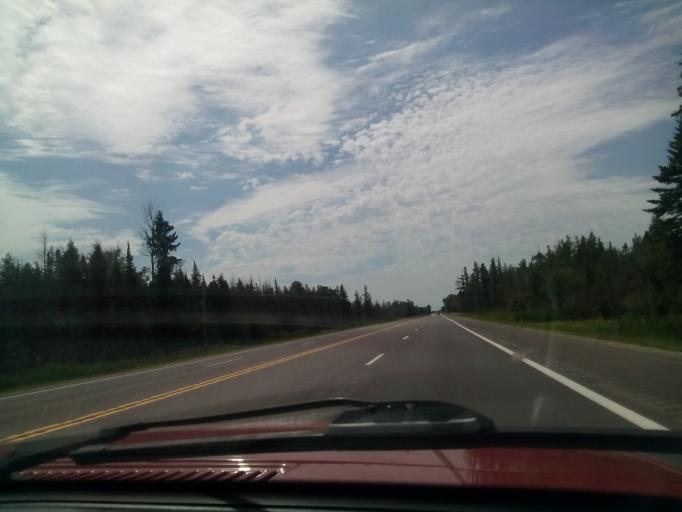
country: US
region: Michigan
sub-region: Schoolcraft County
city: Manistique
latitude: 46.0229
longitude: -85.9862
